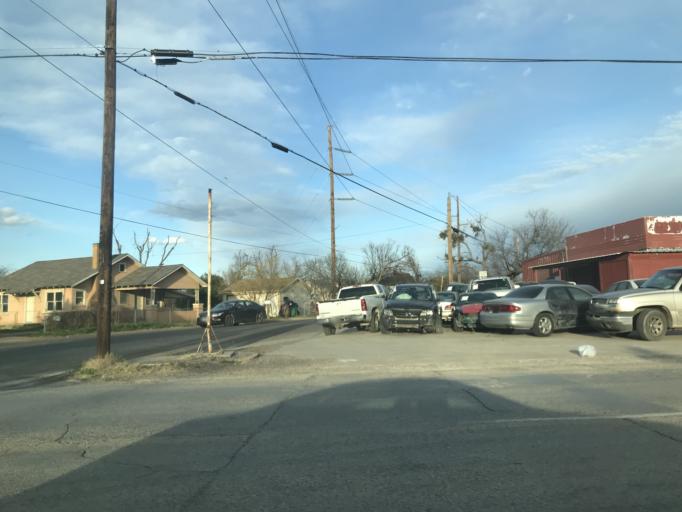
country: US
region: Texas
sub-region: Tom Green County
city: San Angelo
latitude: 31.4973
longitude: -100.4594
